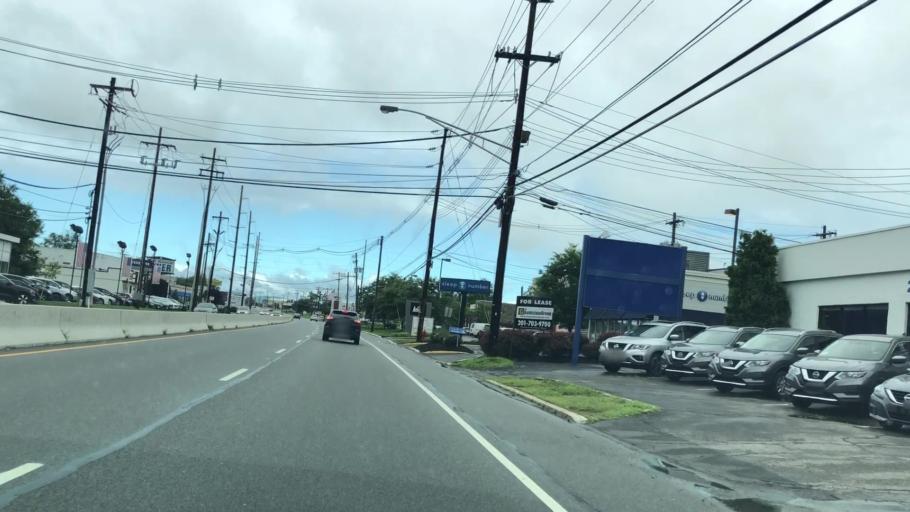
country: US
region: New Jersey
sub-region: Morris County
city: Hanover
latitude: 40.8055
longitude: -74.3687
